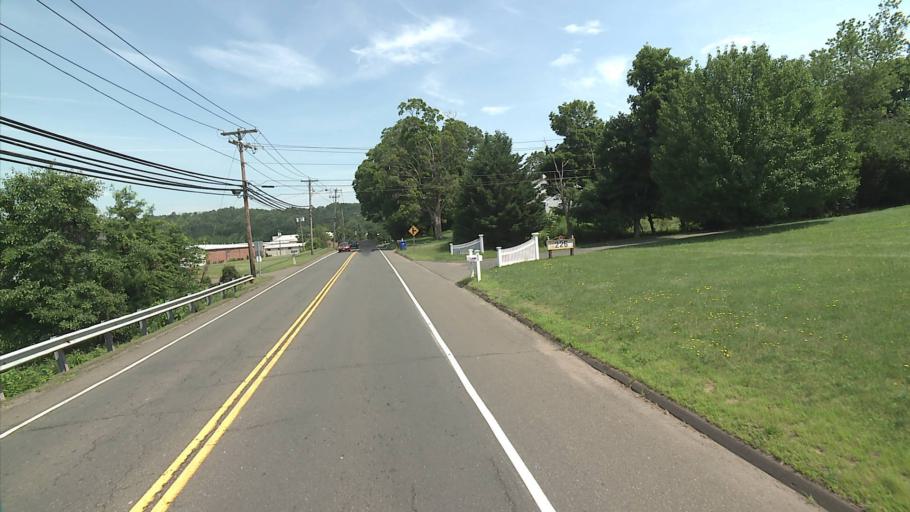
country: US
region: Connecticut
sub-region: New Haven County
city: North Branford
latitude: 41.3199
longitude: -72.7710
